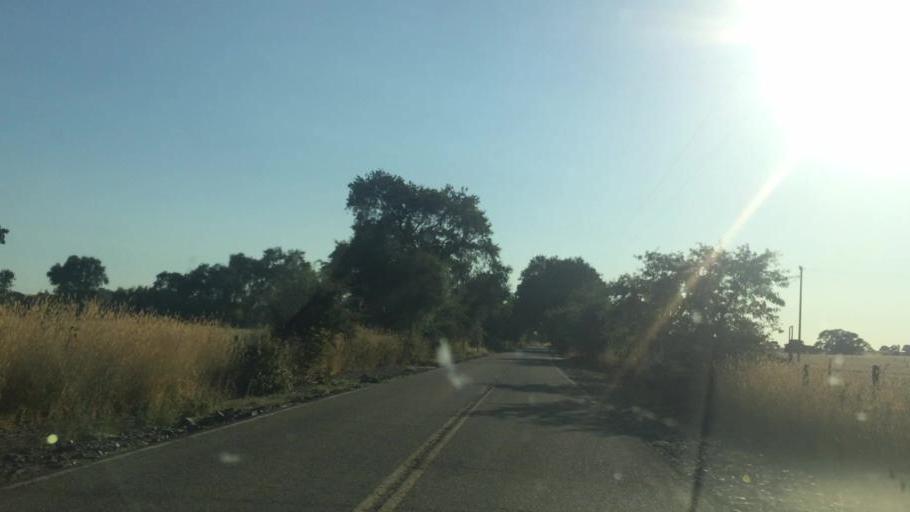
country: US
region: California
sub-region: Amador County
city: Plymouth
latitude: 38.4845
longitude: -120.9198
